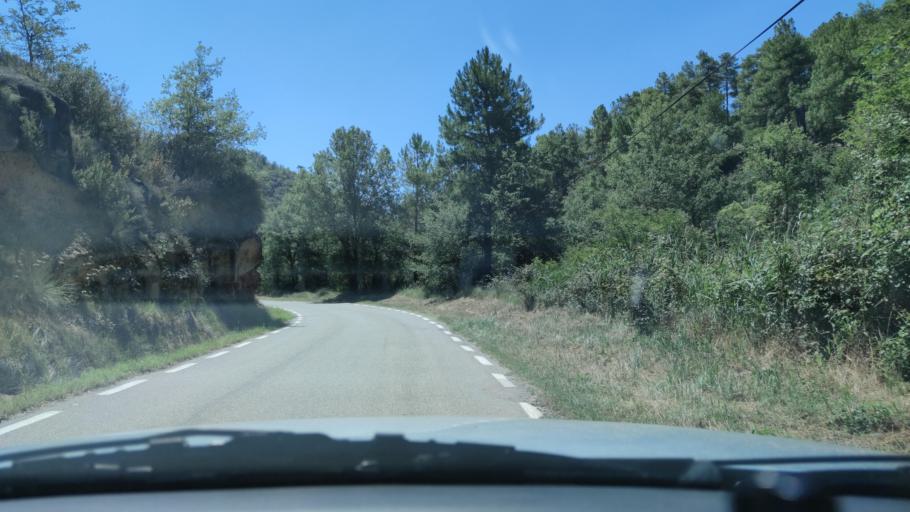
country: ES
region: Catalonia
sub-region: Provincia de Lleida
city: Tora de Riubregos
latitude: 41.8299
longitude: 1.4227
